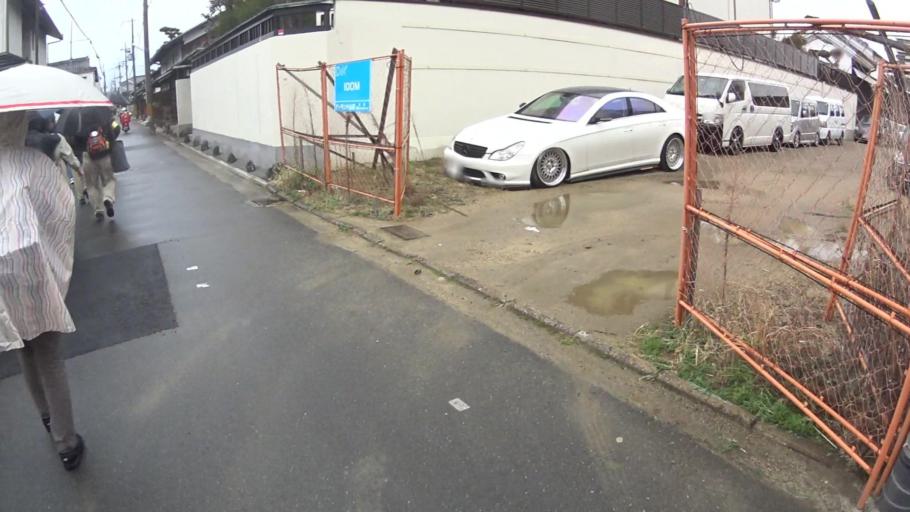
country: JP
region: Kyoto
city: Muko
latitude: 34.9326
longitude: 135.7559
